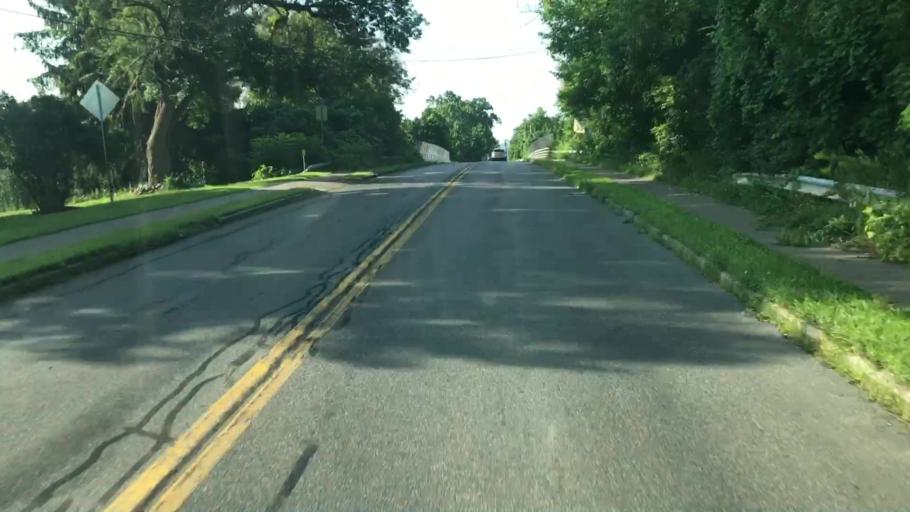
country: US
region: New York
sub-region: Onondaga County
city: Liverpool
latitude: 43.1137
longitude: -76.2053
